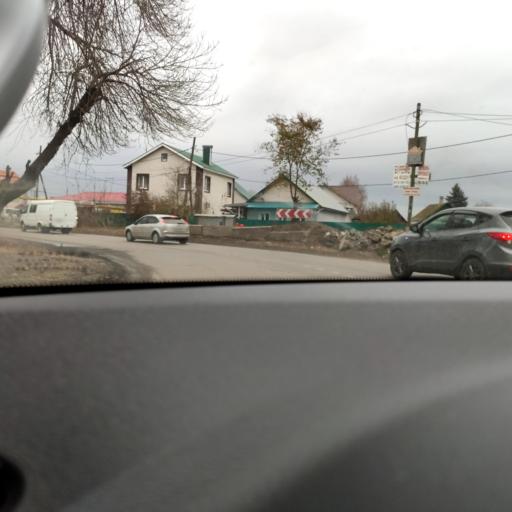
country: RU
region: Samara
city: Smyshlyayevka
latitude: 53.2420
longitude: 50.3369
